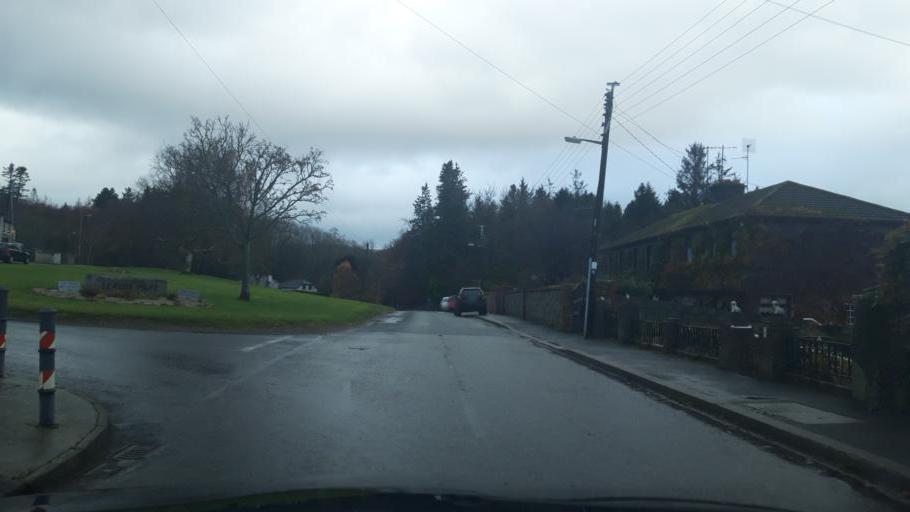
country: IE
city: Newtownmountkennedy
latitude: 53.0952
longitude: -6.1129
